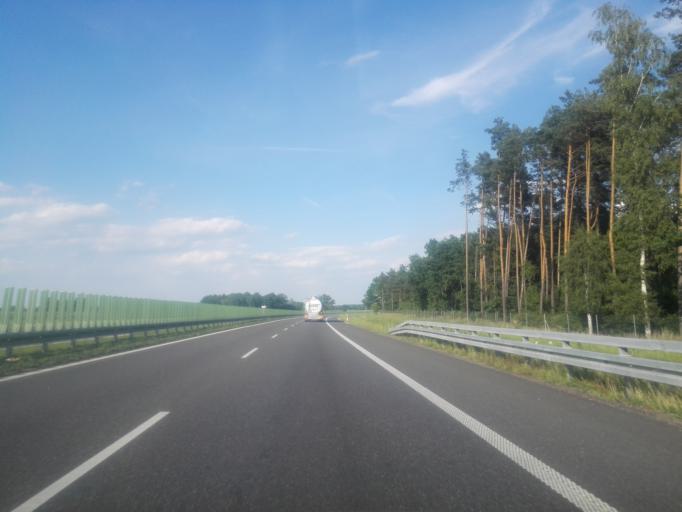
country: PL
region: Lower Silesian Voivodeship
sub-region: Powiat olesnicki
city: Miedzyborz
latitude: 51.3012
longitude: 17.5920
